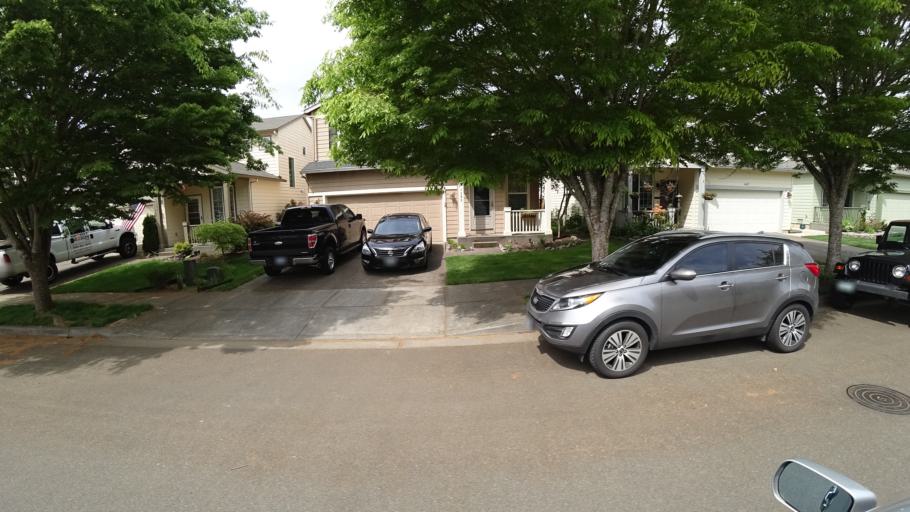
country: US
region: Oregon
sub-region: Washington County
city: Hillsboro
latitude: 45.5350
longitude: -122.9967
